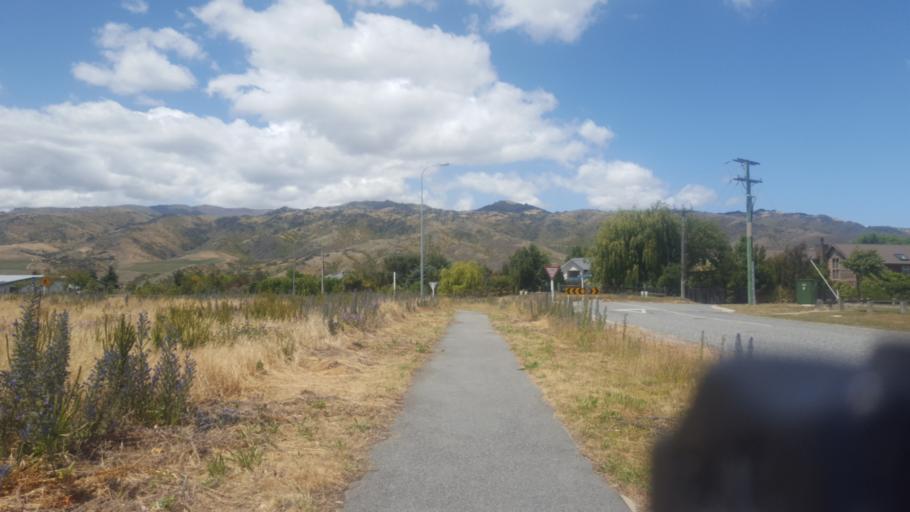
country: NZ
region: Otago
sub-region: Queenstown-Lakes District
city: Wanaka
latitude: -45.0307
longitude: 169.2030
